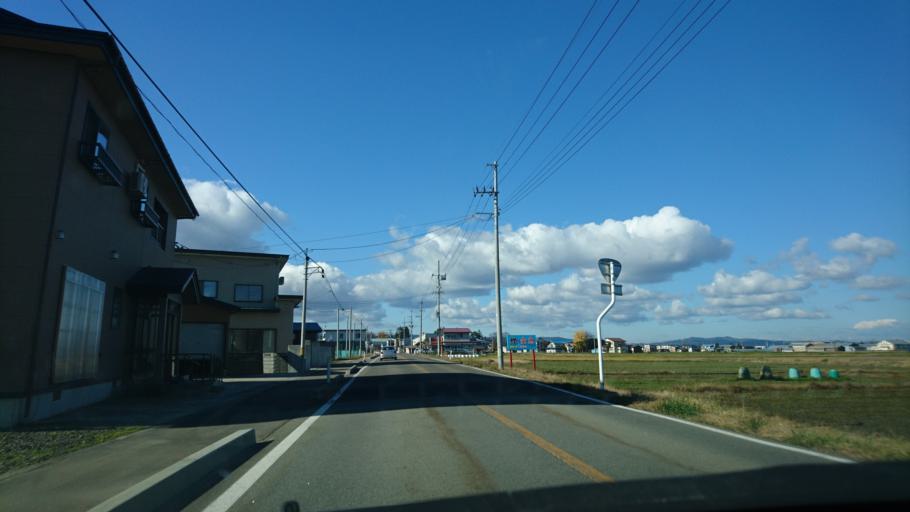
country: JP
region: Akita
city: Yokotemachi
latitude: 39.2741
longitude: 140.4529
